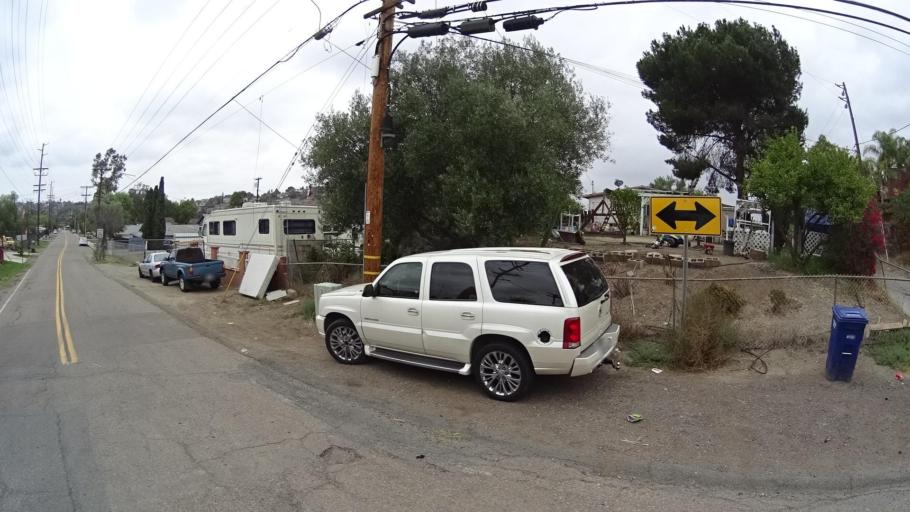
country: US
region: California
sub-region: San Diego County
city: Spring Valley
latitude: 32.7394
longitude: -117.0001
